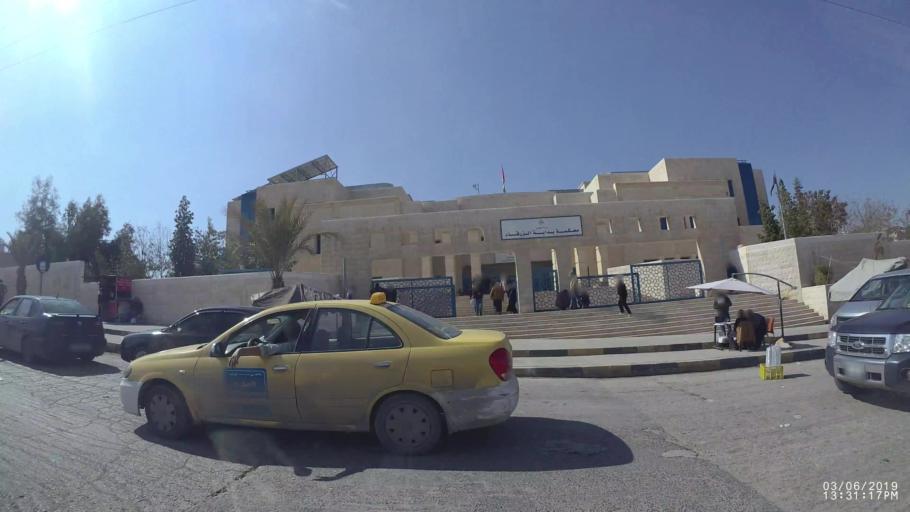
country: JO
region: Zarqa
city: Zarqa
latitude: 32.0760
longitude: 36.1037
